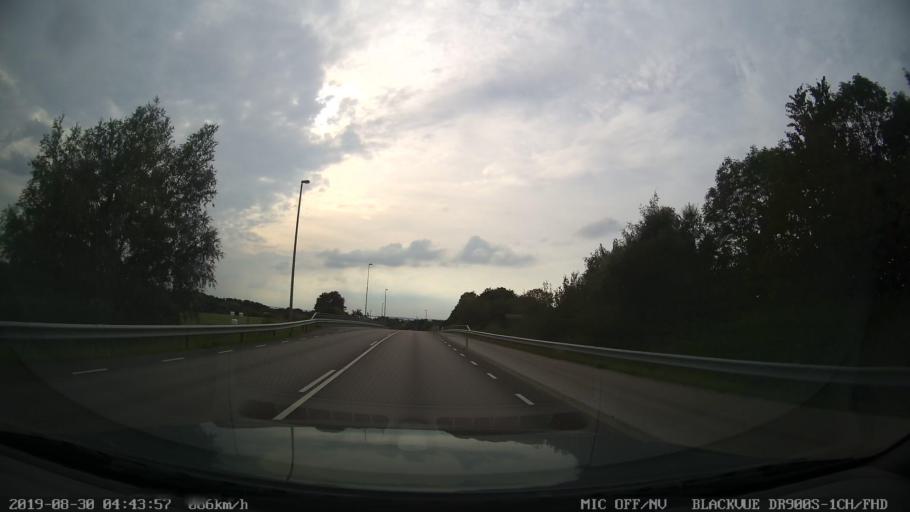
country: SE
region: Skane
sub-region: Helsingborg
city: Rydeback
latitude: 56.0016
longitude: 12.7560
